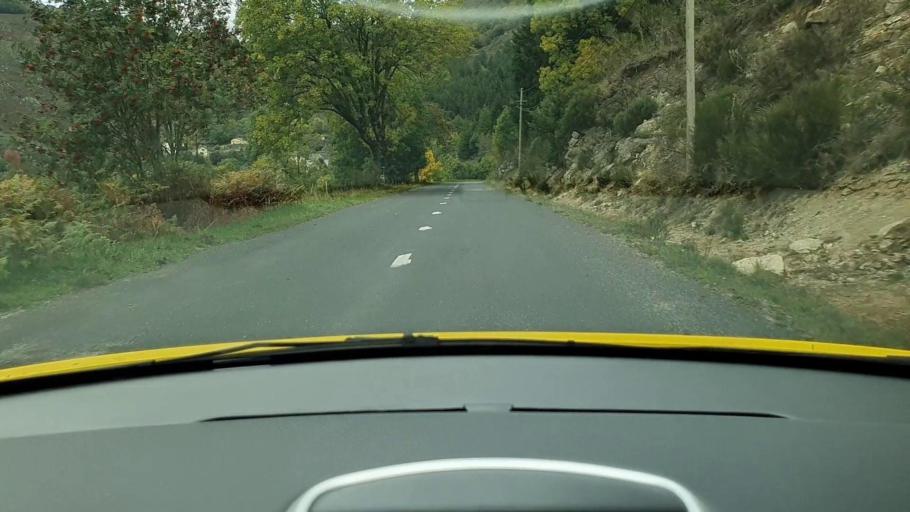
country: FR
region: Languedoc-Roussillon
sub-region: Departement de la Lozere
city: Meyrueis
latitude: 44.0773
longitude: 3.4748
